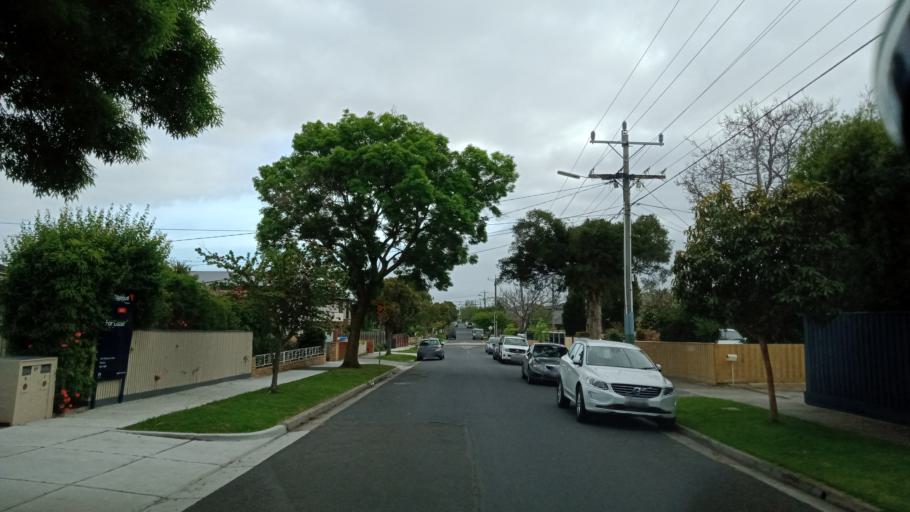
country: AU
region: Victoria
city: Highett
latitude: -37.9336
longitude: 145.0657
